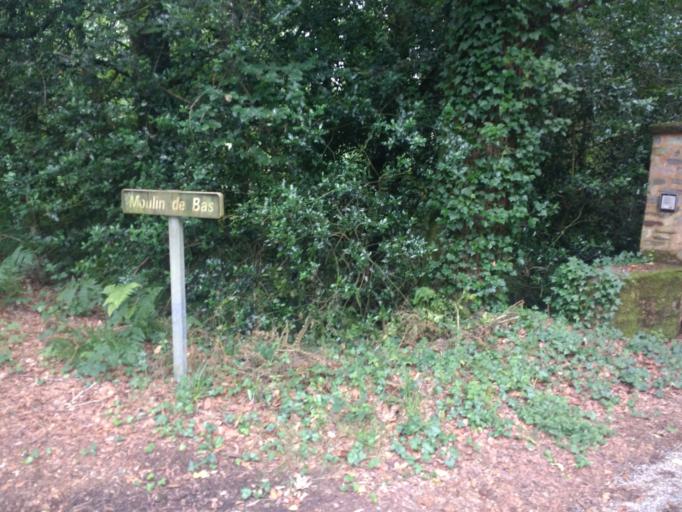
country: FR
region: Brittany
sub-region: Departement d'Ille-et-Vilaine
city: Saint-Just
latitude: 47.7604
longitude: -2.0017
